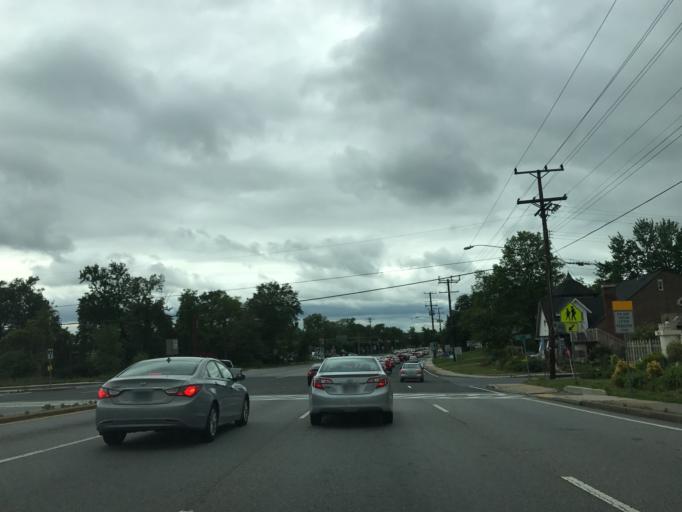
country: US
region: Maryland
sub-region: Prince George's County
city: East Riverdale
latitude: 38.9602
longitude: -76.9171
